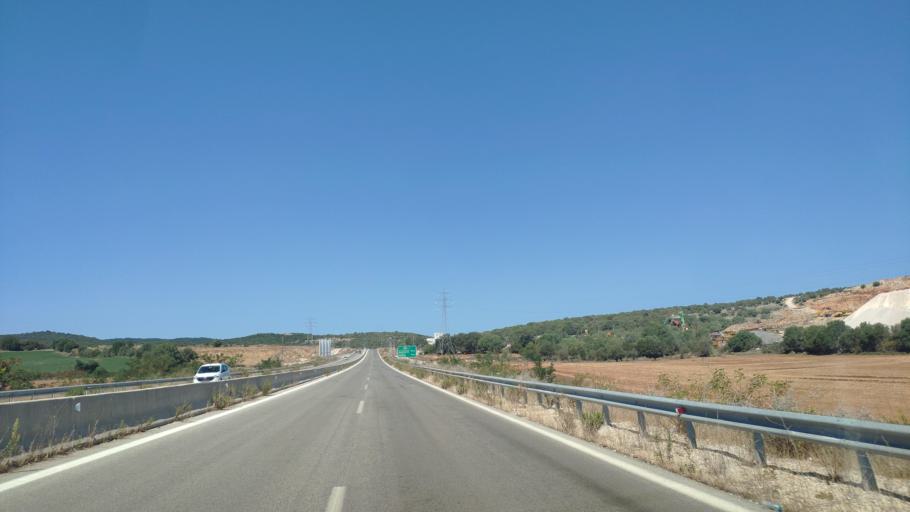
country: GR
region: West Greece
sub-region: Nomos Aitolias kai Akarnanias
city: Vonitsa
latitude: 38.9023
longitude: 20.8664
